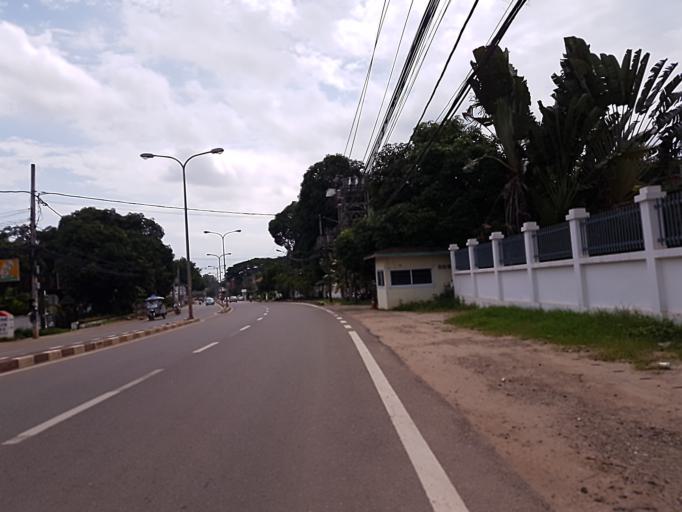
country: LA
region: Vientiane
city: Vientiane
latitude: 17.9343
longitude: 102.6167
